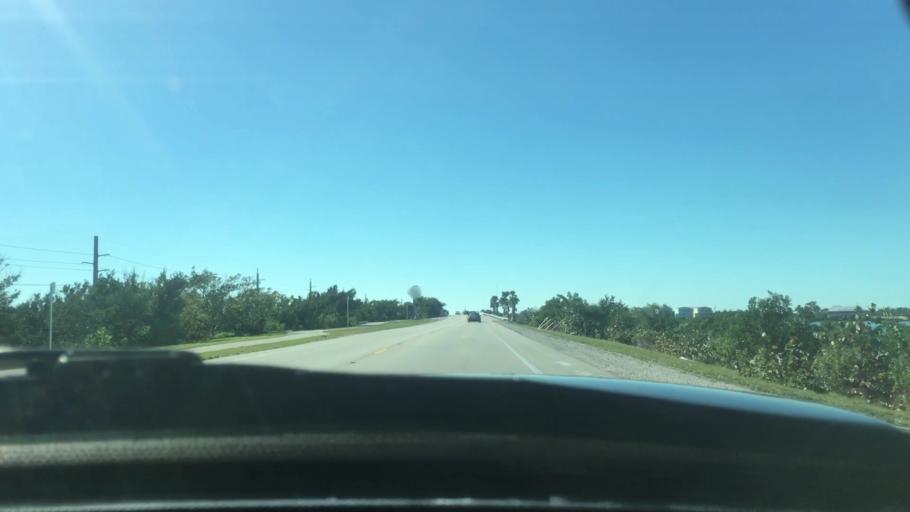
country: US
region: Florida
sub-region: Monroe County
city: Big Pine Key
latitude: 24.6681
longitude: -81.3809
